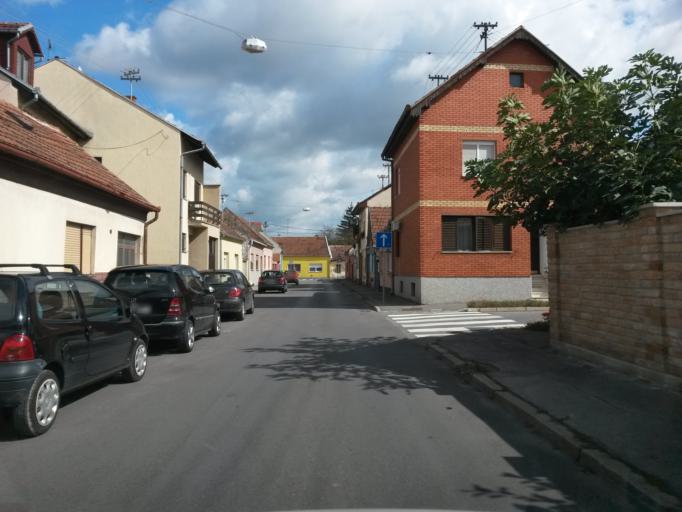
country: HR
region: Osjecko-Baranjska
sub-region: Grad Osijek
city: Osijek
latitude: 45.5604
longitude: 18.6574
